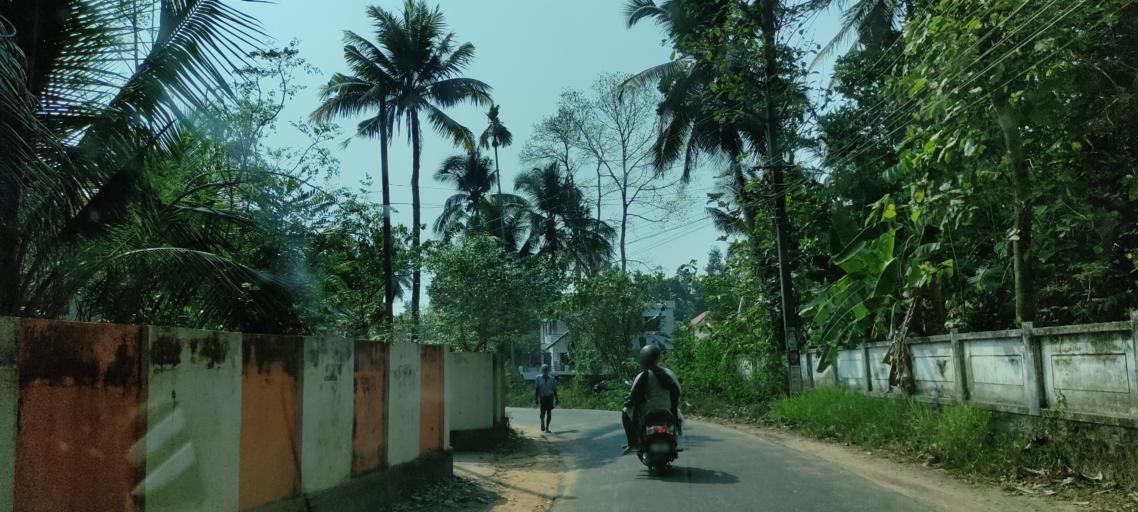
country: IN
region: Kerala
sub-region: Pattanamtitta
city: Tiruvalla
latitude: 9.3456
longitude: 76.5377
